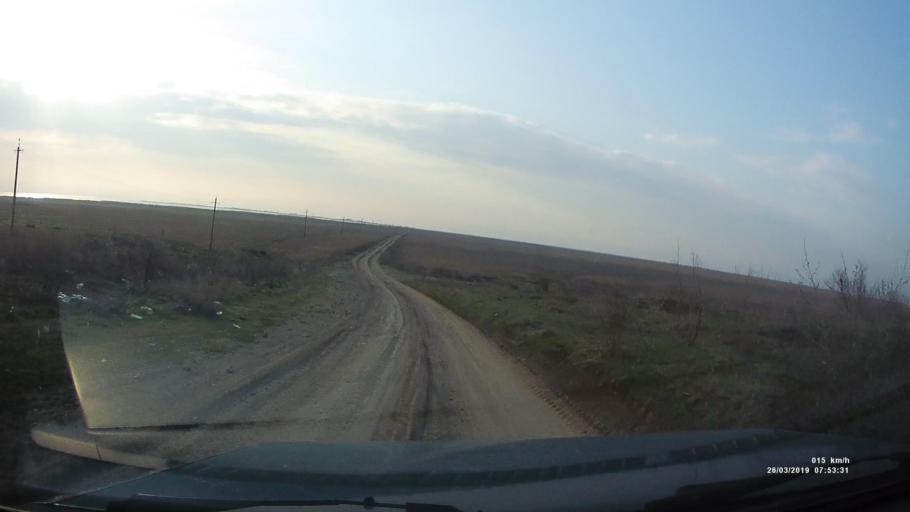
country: RU
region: Krasnodarskiy
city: Shabel'skoye
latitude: 47.1354
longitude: 38.5488
